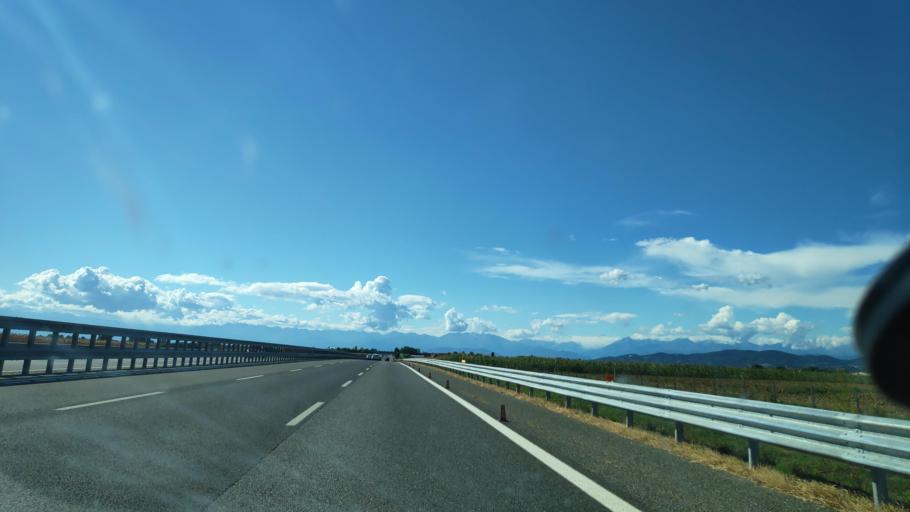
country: IT
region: Piedmont
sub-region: Provincia di Torino
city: Riva Presso Chieri
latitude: 44.9550
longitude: 7.8963
